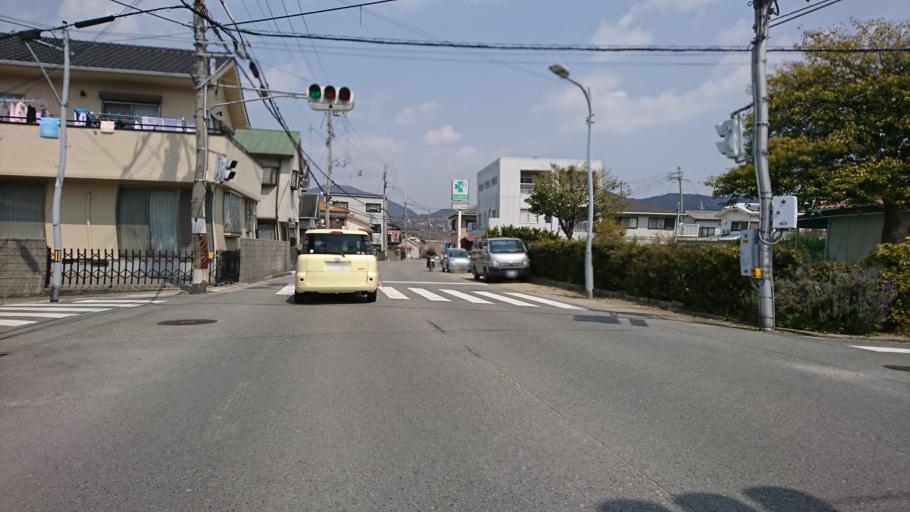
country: JP
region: Hyogo
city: Kakogawacho-honmachi
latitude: 34.7891
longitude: 134.7900
